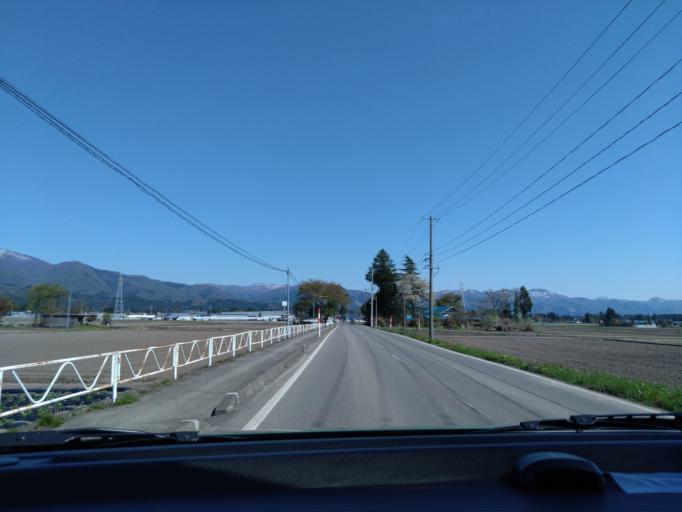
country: JP
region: Akita
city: Kakunodatemachi
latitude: 39.5736
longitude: 140.5755
